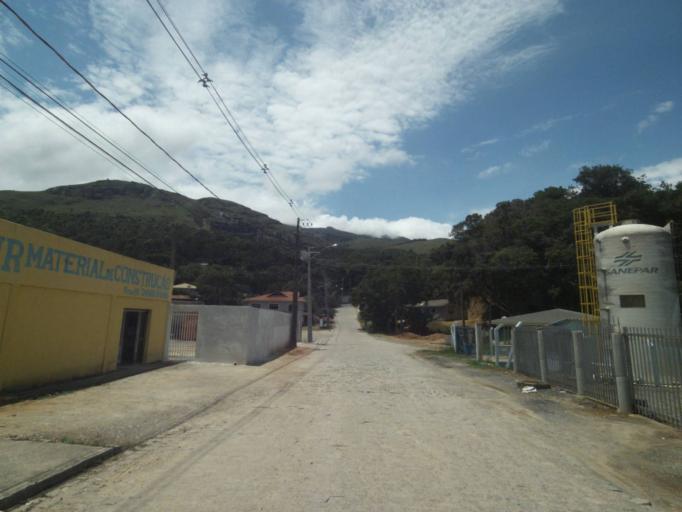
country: BR
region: Parana
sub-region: Campina Grande Do Sul
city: Campina Grande do Sul
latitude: -25.1094
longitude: -48.8356
